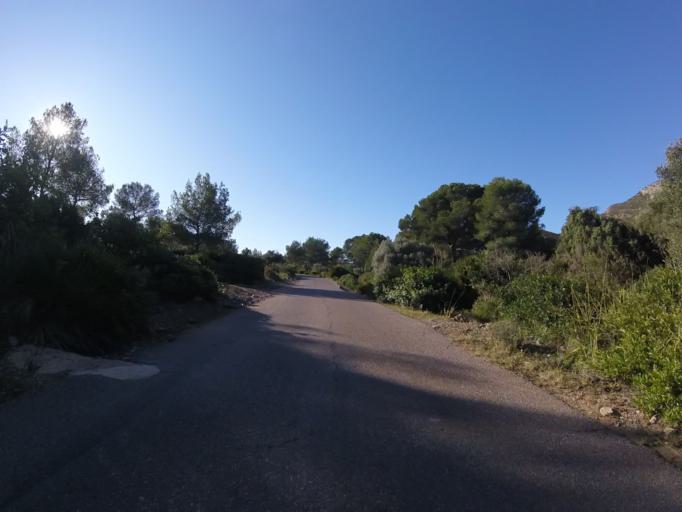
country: ES
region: Valencia
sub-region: Provincia de Castello
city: Orpesa/Oropesa del Mar
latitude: 40.0878
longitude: 0.1250
